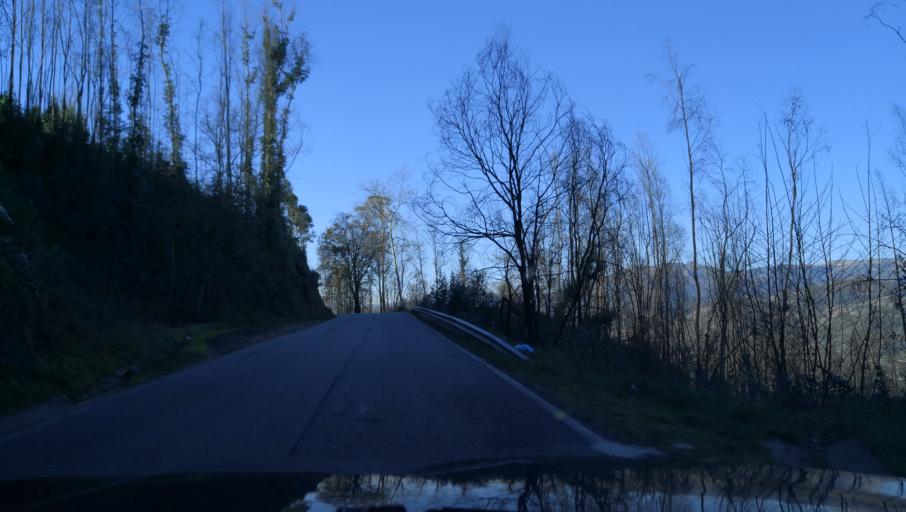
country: PT
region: Viseu
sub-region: Vouzela
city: Vouzela
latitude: 40.7298
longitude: -8.1403
